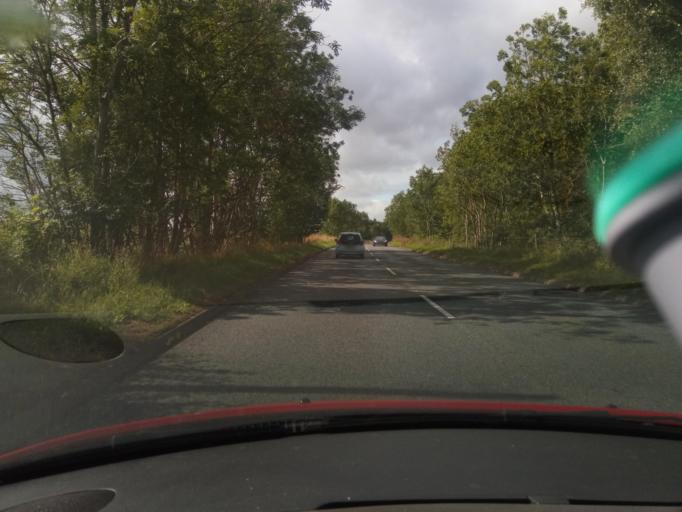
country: GB
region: Scotland
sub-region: The Scottish Borders
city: Saint Boswells
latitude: 55.5686
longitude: -2.5831
